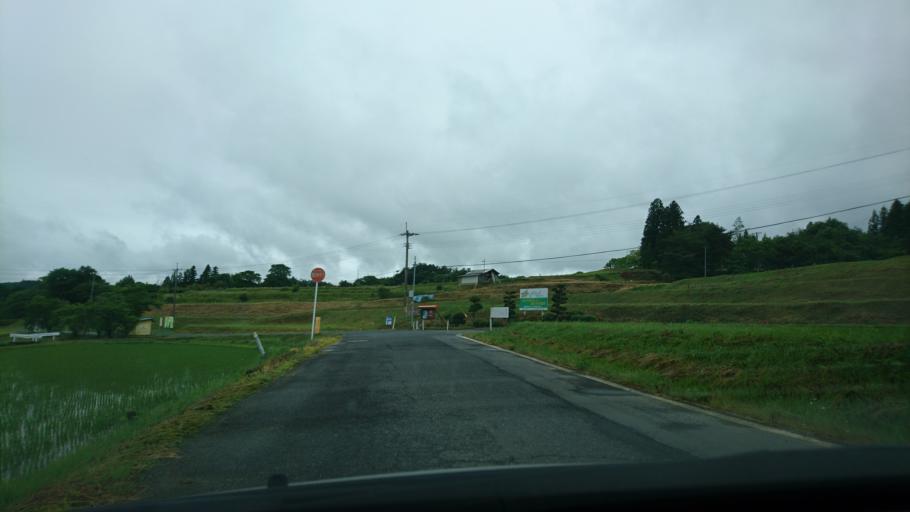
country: JP
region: Iwate
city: Ichinoseki
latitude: 38.9251
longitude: 141.2094
